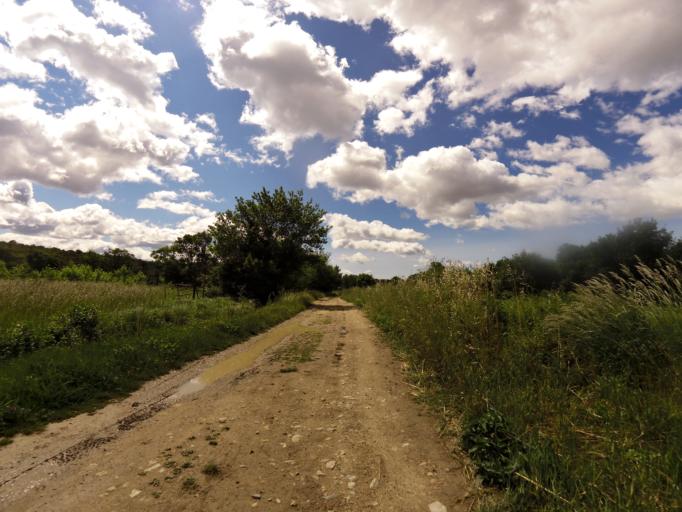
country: FR
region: Languedoc-Roussillon
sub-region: Departement du Gard
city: Vergeze
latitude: 43.7624
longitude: 4.2129
